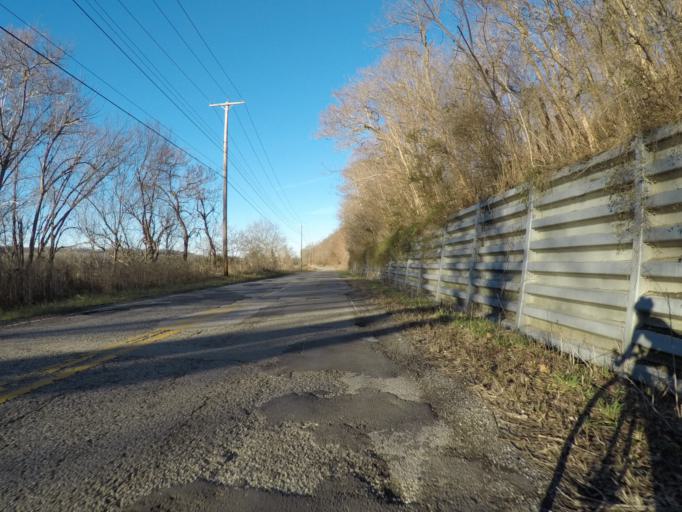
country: US
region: Kentucky
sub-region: Boyd County
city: Catlettsburg
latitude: 38.3889
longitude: -82.5934
